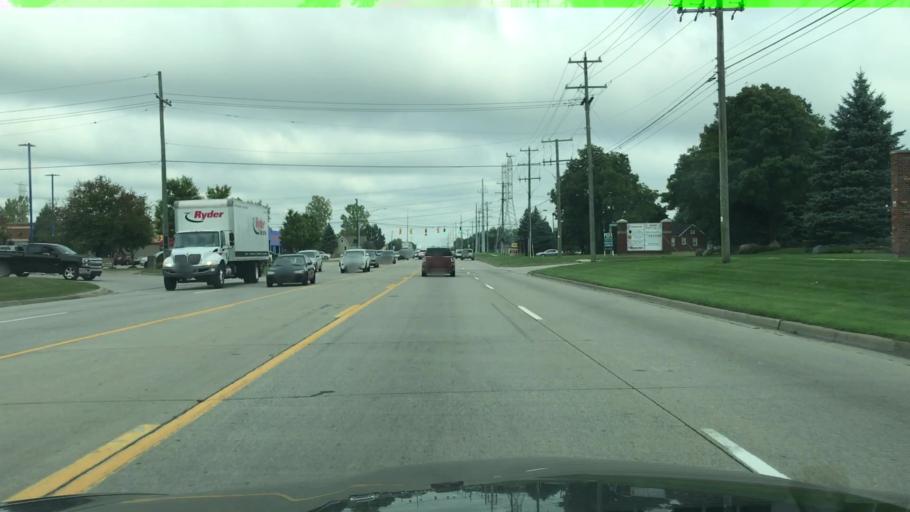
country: US
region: Michigan
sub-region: Macomb County
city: Shelby
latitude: 42.6698
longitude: -83.0091
